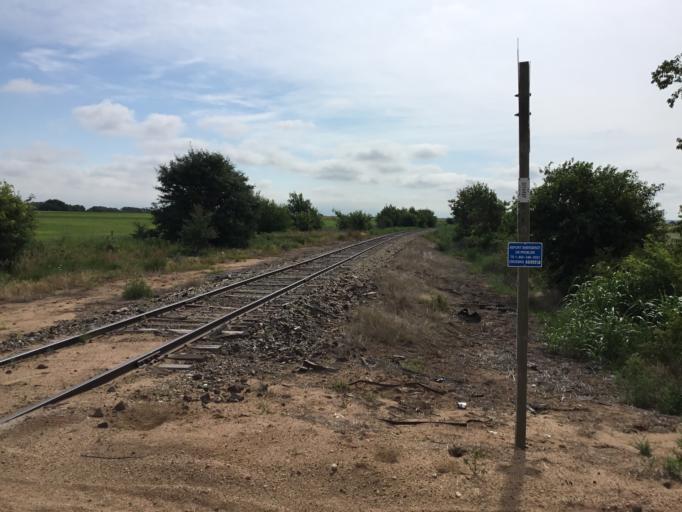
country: US
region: Kansas
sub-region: Kingman County
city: Kingman
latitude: 37.4461
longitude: -98.2638
